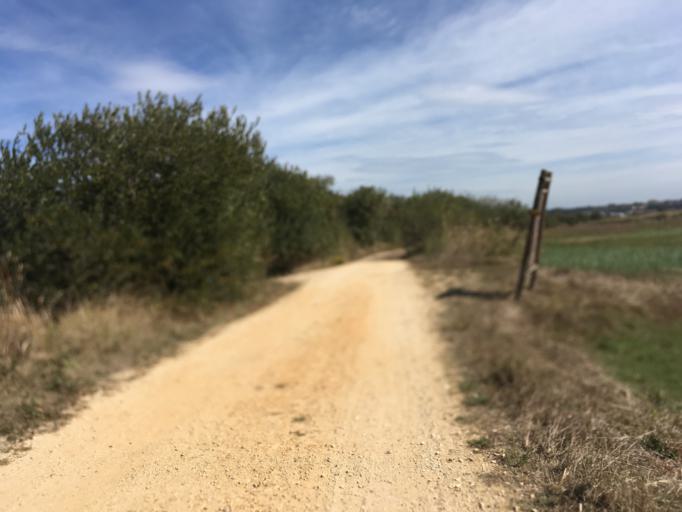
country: PT
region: Aveiro
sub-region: Estarreja
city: Salreu
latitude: 40.7333
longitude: -8.5811
